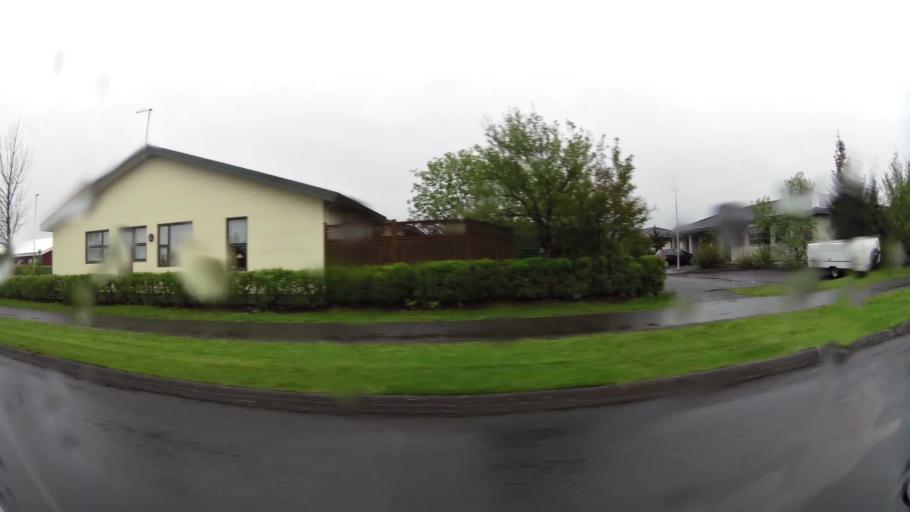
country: IS
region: South
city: Selfoss
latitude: 63.9273
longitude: -20.9916
